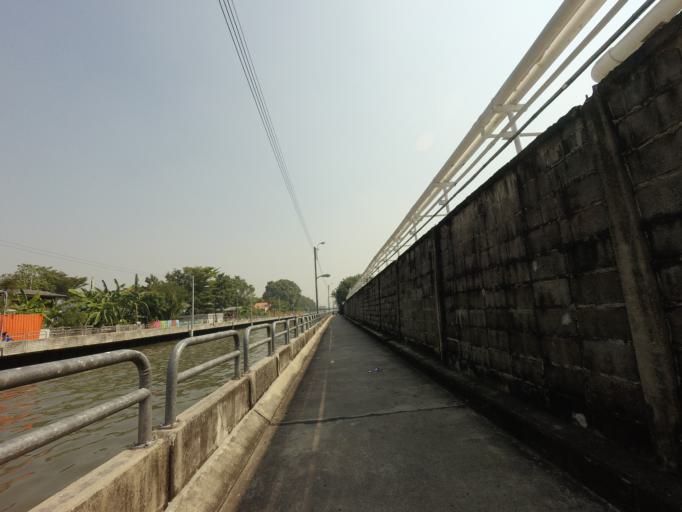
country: TH
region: Bangkok
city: Bang Kapi
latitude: 13.7715
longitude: 100.6579
